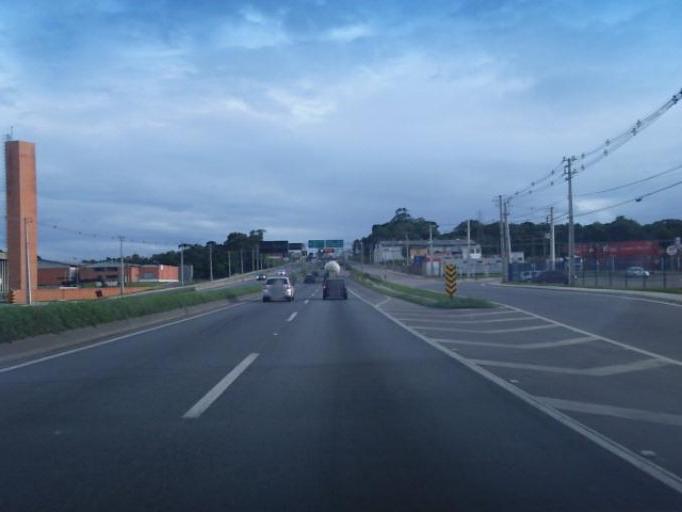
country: BR
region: Parana
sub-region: Sao Jose Dos Pinhais
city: Sao Jose dos Pinhais
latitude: -25.5754
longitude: -49.1797
